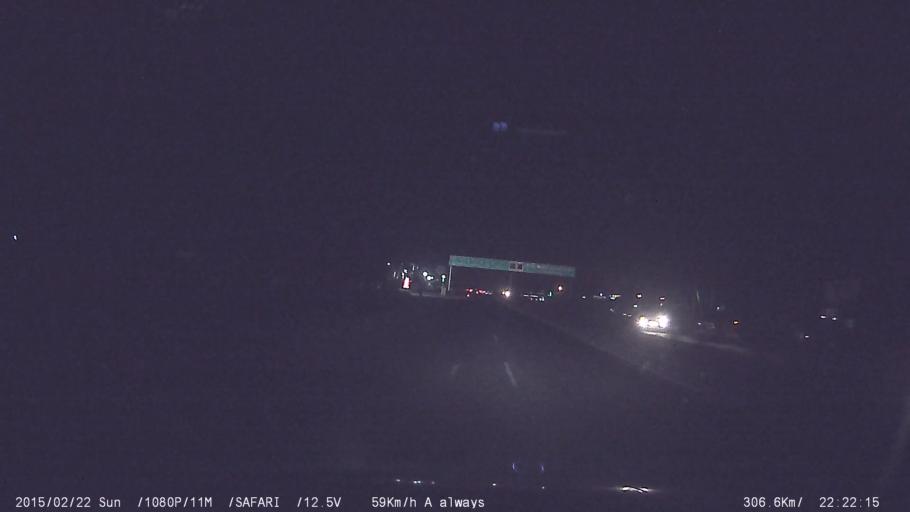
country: IN
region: Tamil Nadu
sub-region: Karur
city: Karur
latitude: 11.0121
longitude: 78.0683
